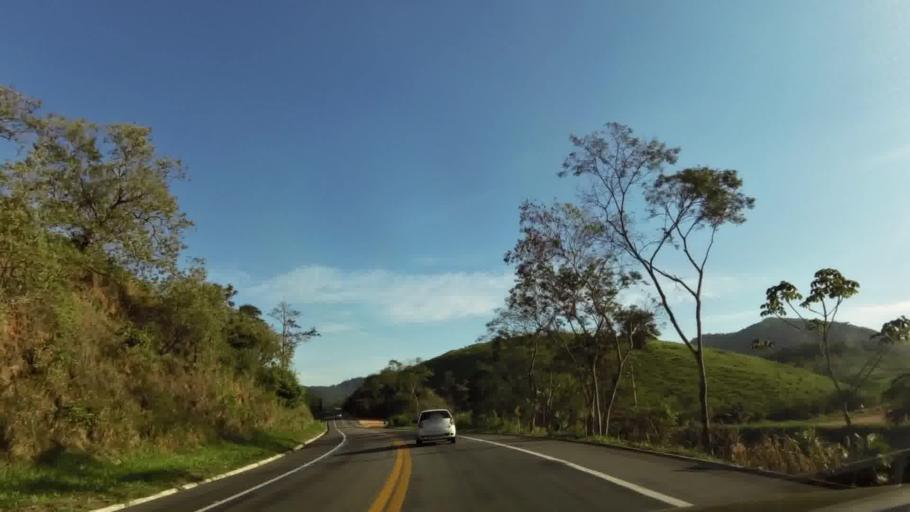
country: BR
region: Espirito Santo
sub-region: Viana
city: Viana
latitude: -20.4011
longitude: -40.4555
